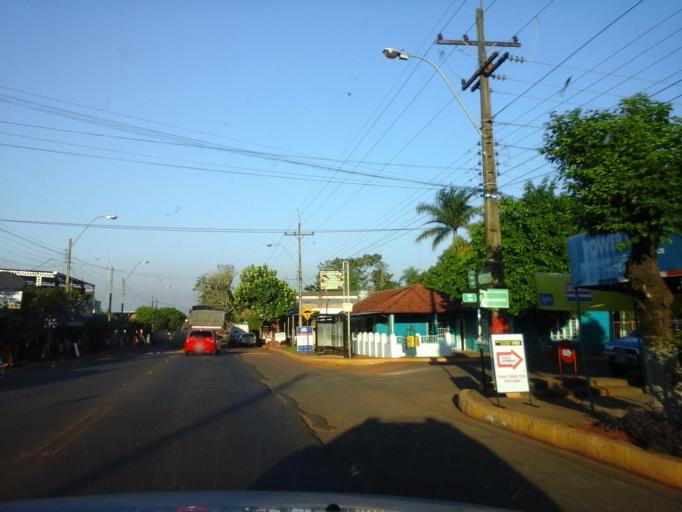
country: PY
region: Itapua
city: General Delgado
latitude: -27.0896
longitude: -56.5234
